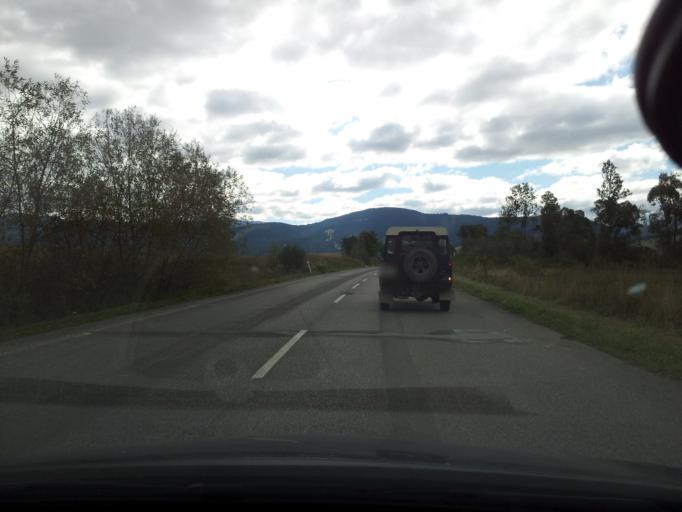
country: SK
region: Zilinsky
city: Ruzomberok
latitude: 49.0754
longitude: 19.4384
